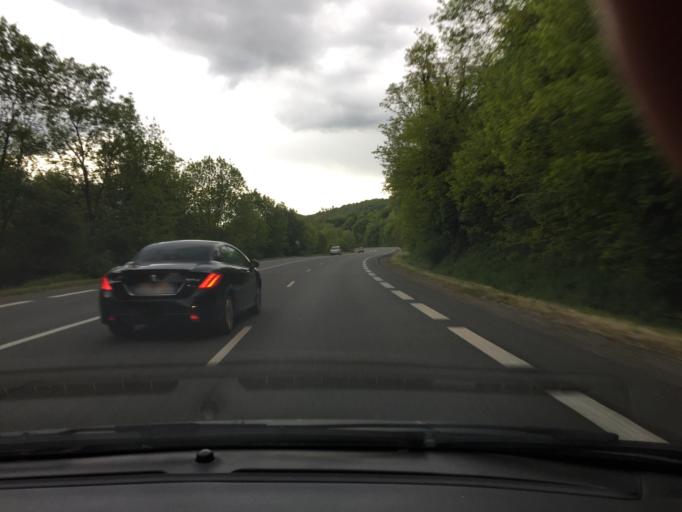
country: FR
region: Rhone-Alpes
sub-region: Departement du Rhone
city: Montagny
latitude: 45.6369
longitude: 4.7561
